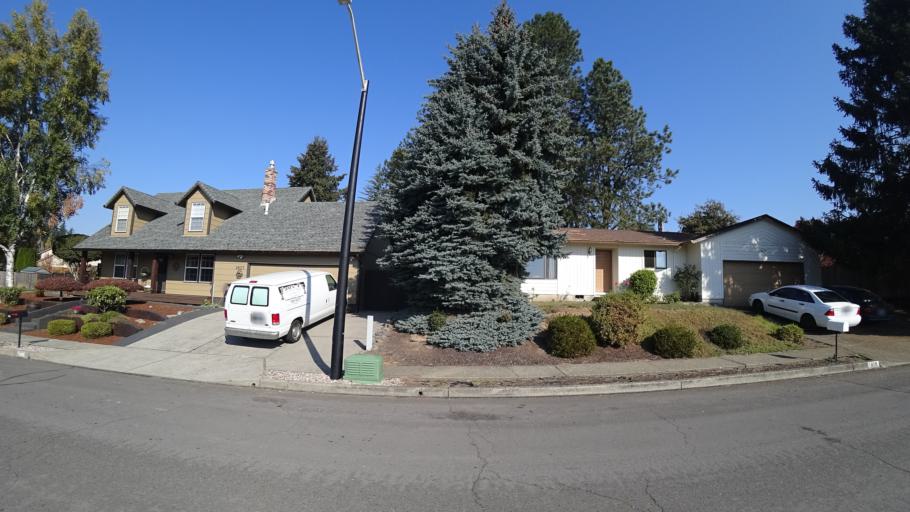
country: US
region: Oregon
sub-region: Multnomah County
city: Gresham
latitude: 45.4944
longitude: -122.4498
